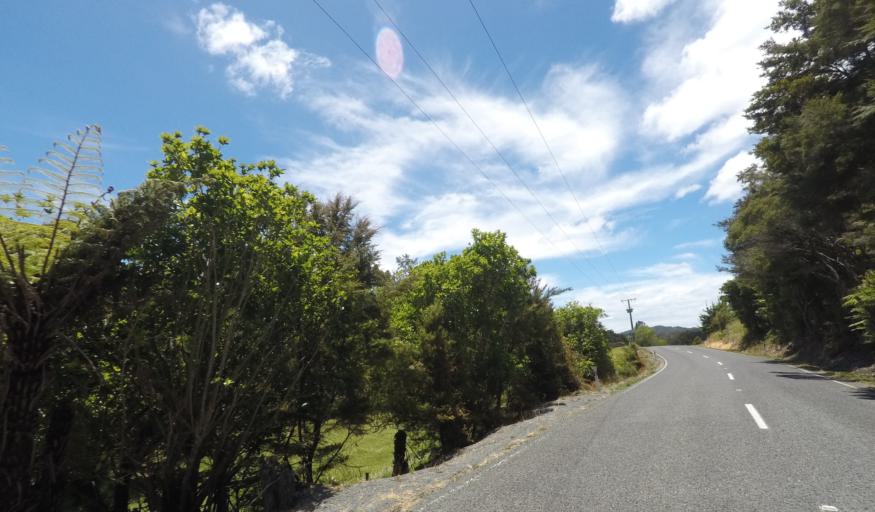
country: NZ
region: Northland
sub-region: Whangarei
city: Ngunguru
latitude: -35.5076
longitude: 174.4002
